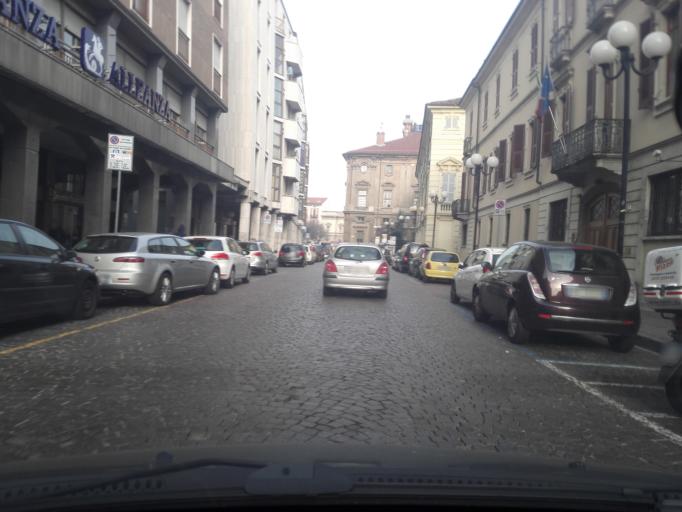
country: IT
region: Piedmont
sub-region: Provincia di Alessandria
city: Alessandria
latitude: 44.9117
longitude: 8.6165
